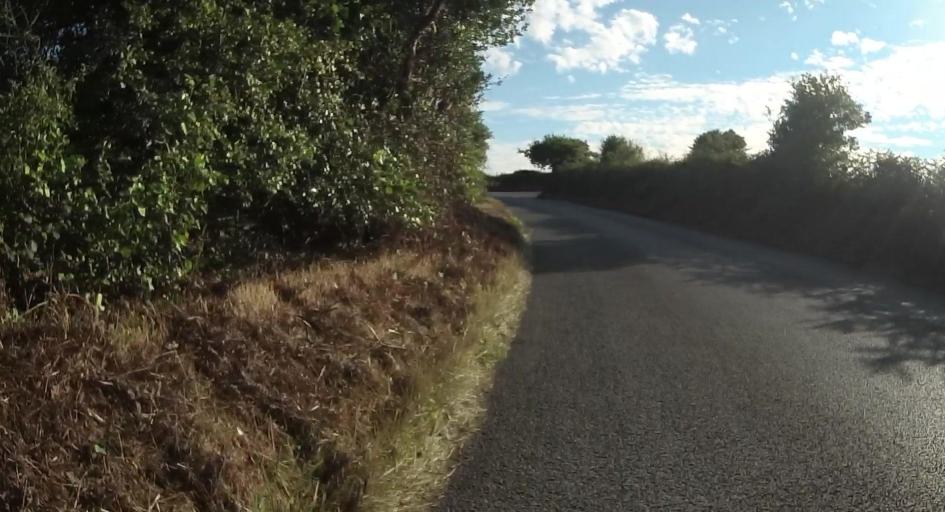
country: GB
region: England
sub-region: Isle of Wight
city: Newport
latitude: 50.6455
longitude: -1.2749
